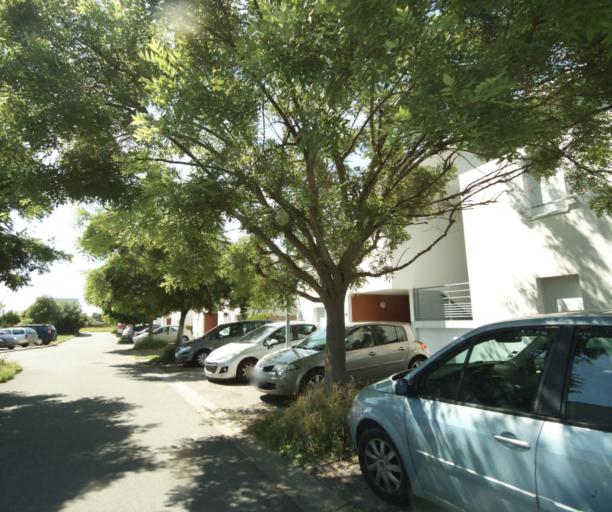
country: FR
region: Pays de la Loire
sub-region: Departement de la Mayenne
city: Change
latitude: 48.0807
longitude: -0.7891
